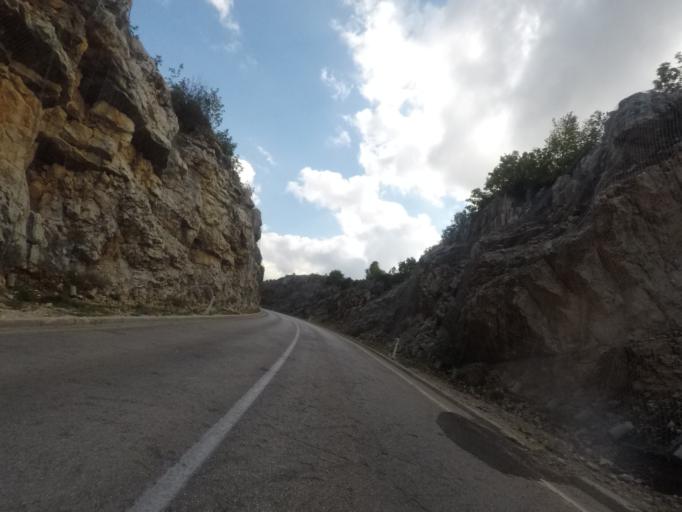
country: BA
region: Republika Srpska
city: Trebinje
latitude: 42.6492
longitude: 18.3694
